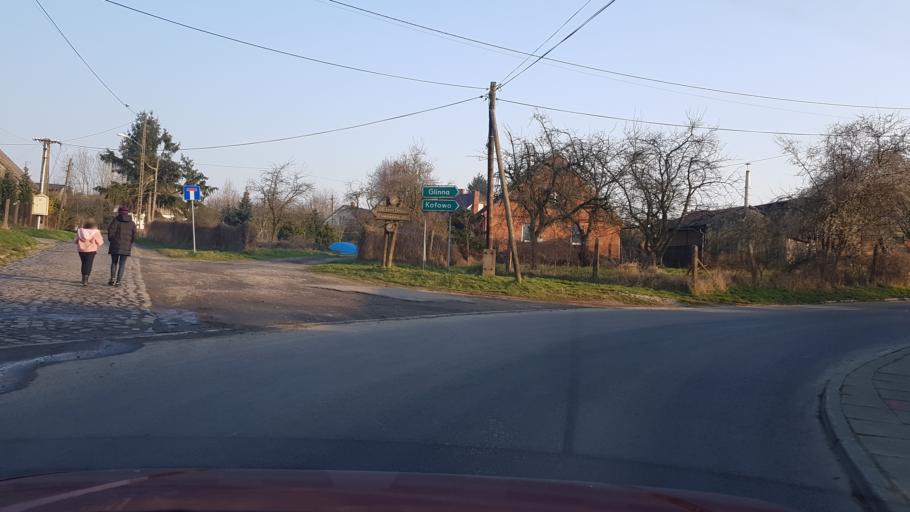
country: PL
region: West Pomeranian Voivodeship
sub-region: Powiat gryfinski
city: Stare Czarnowo
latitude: 53.3389
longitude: 14.7500
